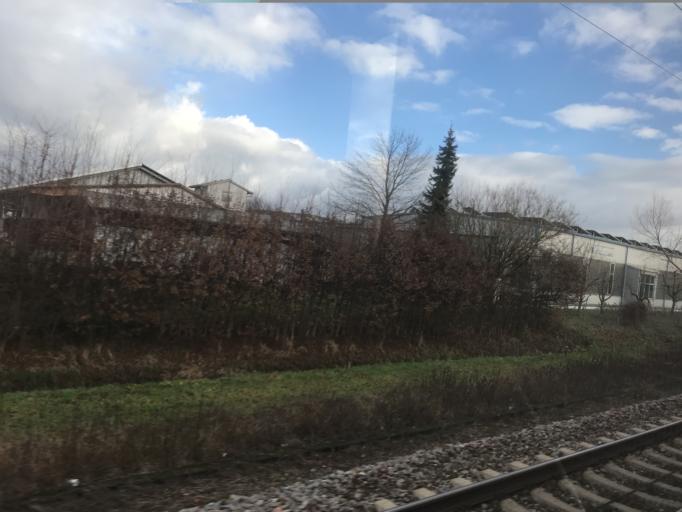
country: DE
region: Baden-Wuerttemberg
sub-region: Freiburg Region
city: Riegel
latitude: 48.1498
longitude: 7.7737
